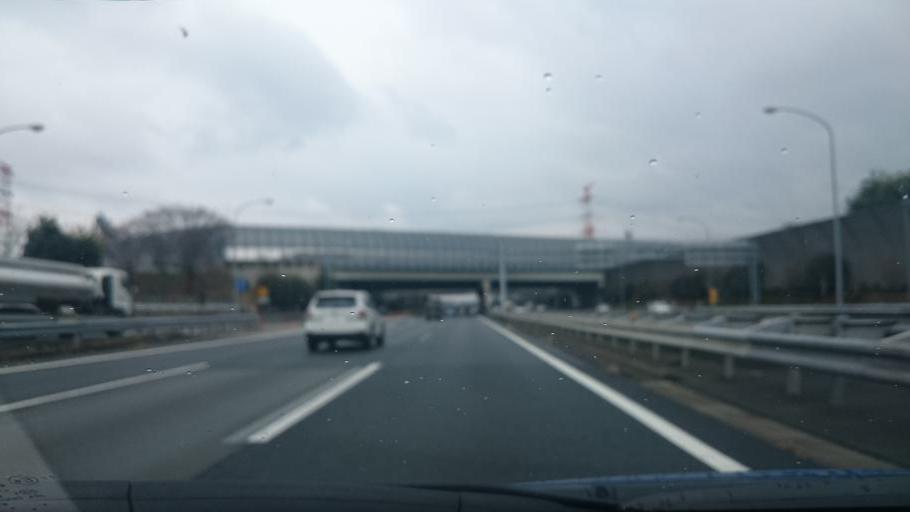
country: JP
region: Saitama
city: Sakado
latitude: 35.9336
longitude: 139.4066
